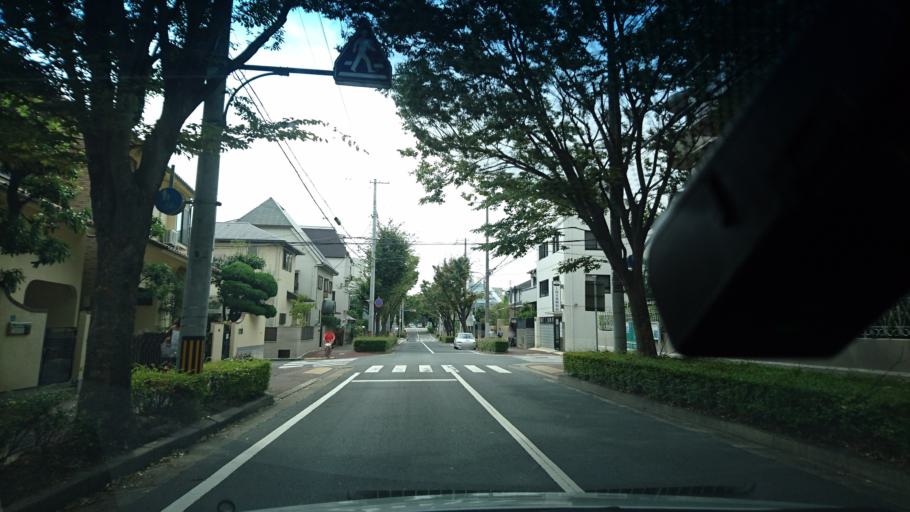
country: JP
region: Hyogo
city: Ashiya
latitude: 34.7318
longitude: 135.3146
